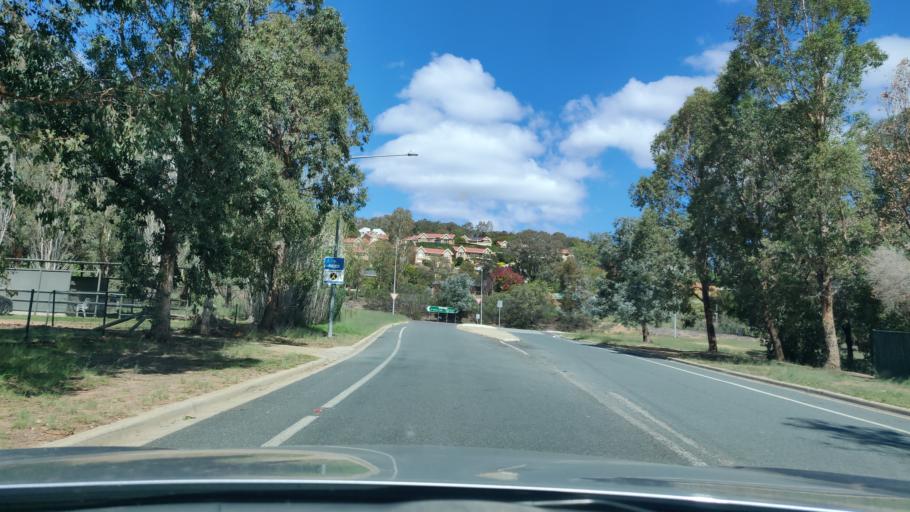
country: AU
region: Australian Capital Territory
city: Macarthur
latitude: -35.4429
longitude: 149.1018
